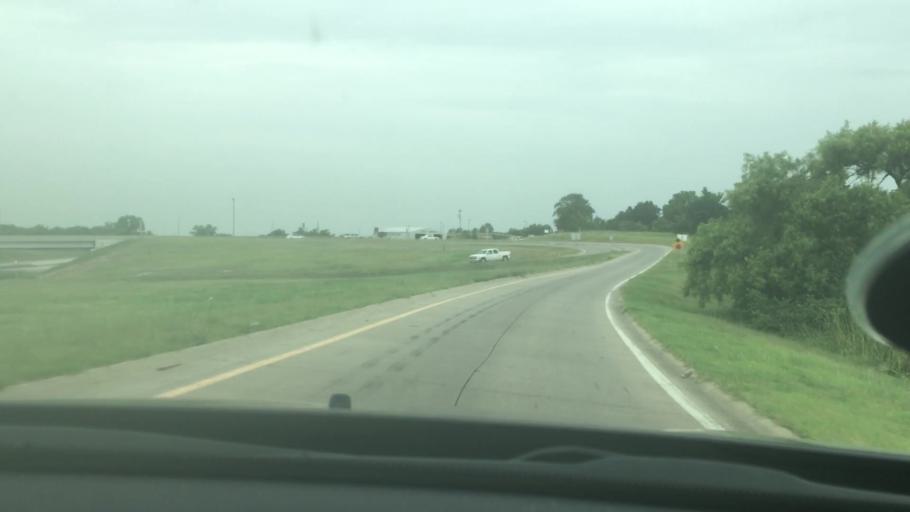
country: US
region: Oklahoma
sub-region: Pontotoc County
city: Ada
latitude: 34.7628
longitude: -96.6996
